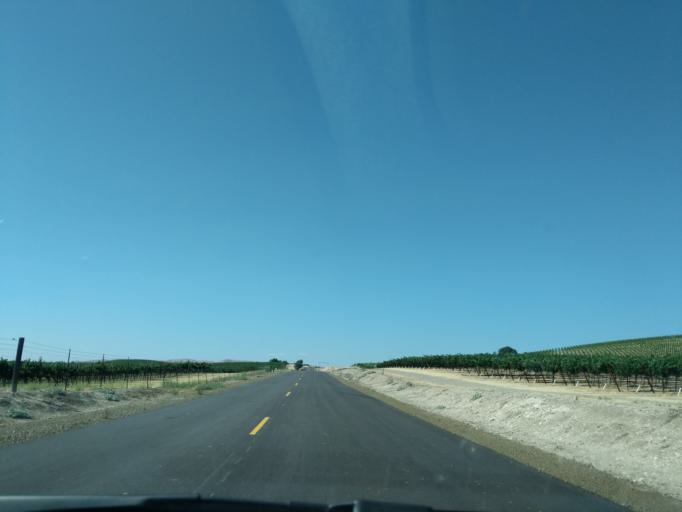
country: US
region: California
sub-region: San Luis Obispo County
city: San Miguel
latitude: 35.6981
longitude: -120.6406
